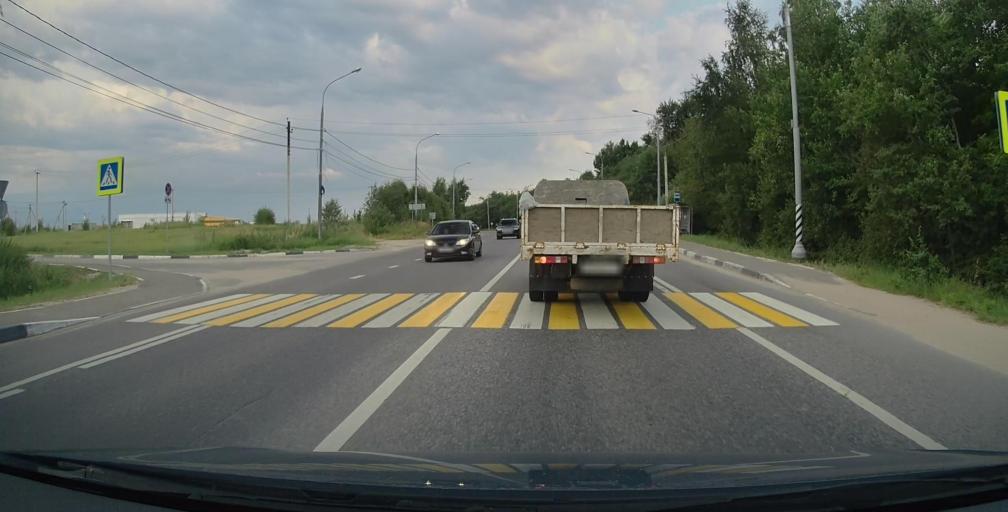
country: RU
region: Moskovskaya
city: Skoropuskovskiy
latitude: 56.3790
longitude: 38.1073
